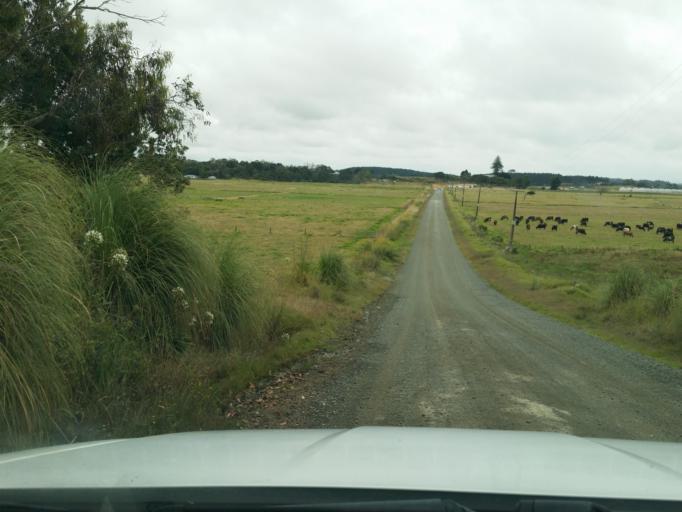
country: NZ
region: Northland
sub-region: Kaipara District
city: Dargaville
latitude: -36.0134
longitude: 173.8925
